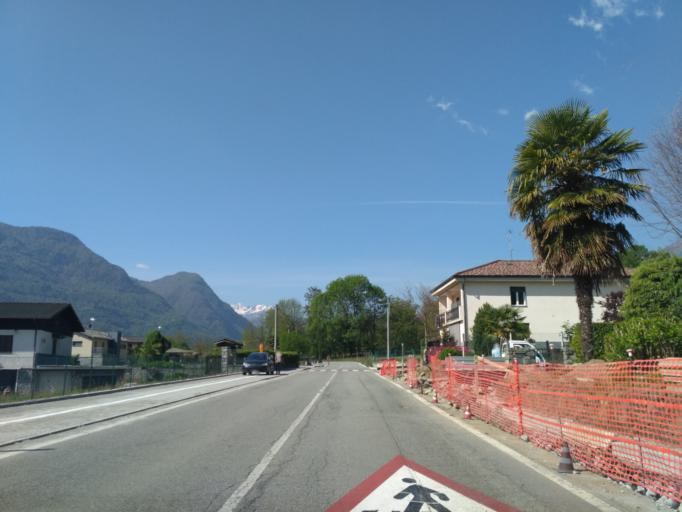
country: IT
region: Lombardy
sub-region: Provincia di Sondrio
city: Villapinta
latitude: 46.1736
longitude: 9.7056
